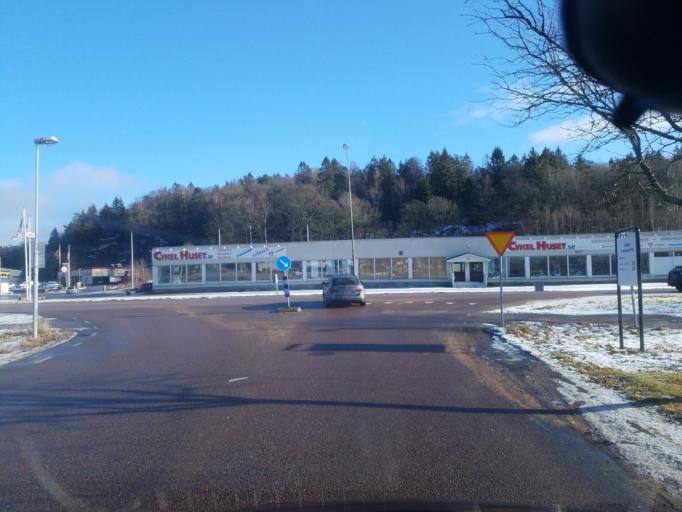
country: SE
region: Vaestra Goetaland
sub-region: Uddevalla Kommun
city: Uddevalla
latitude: 58.3505
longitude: 11.8501
